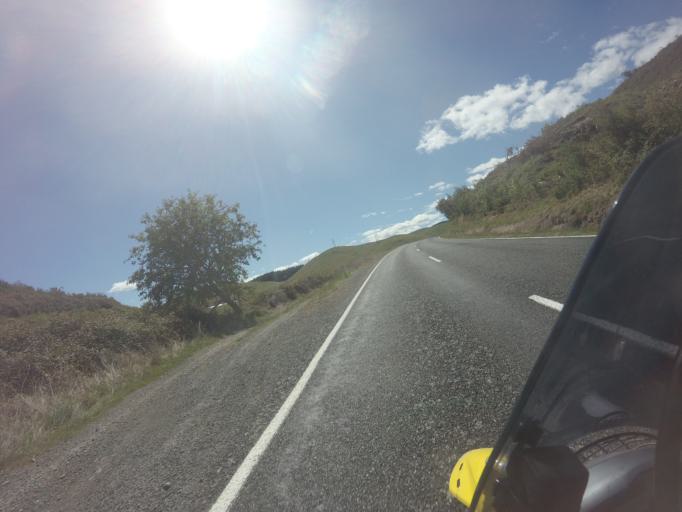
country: NZ
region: Bay of Plenty
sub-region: Whakatane District
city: Murupara
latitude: -38.3036
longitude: 176.8126
